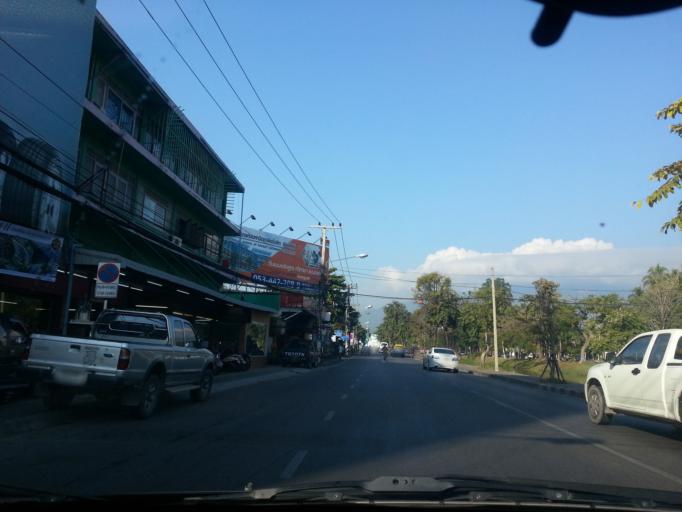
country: TH
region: Chiang Mai
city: Chiang Mai
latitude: 18.7813
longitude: 98.9814
